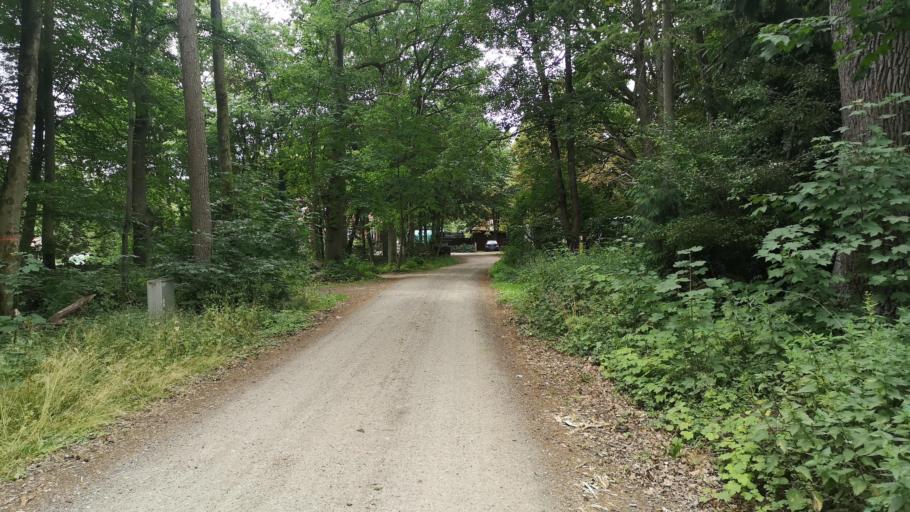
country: DE
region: Lower Saxony
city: Thomasburg
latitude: 53.2397
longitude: 10.7016
